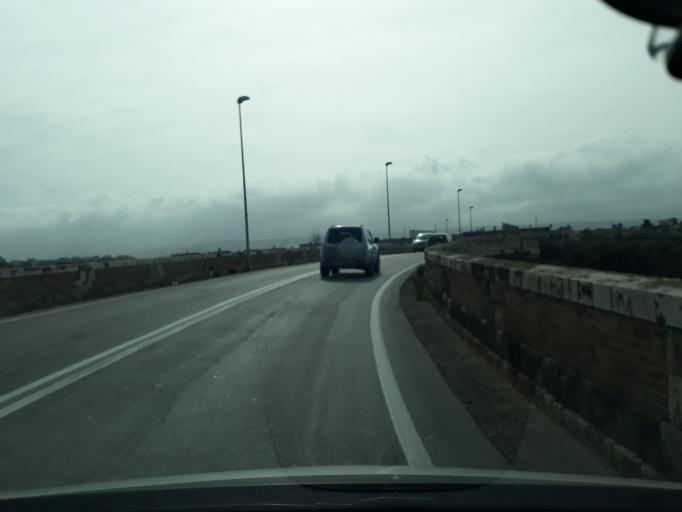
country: IT
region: Apulia
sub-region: Provincia di Bari
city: Monopoli
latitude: 40.9573
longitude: 17.2828
